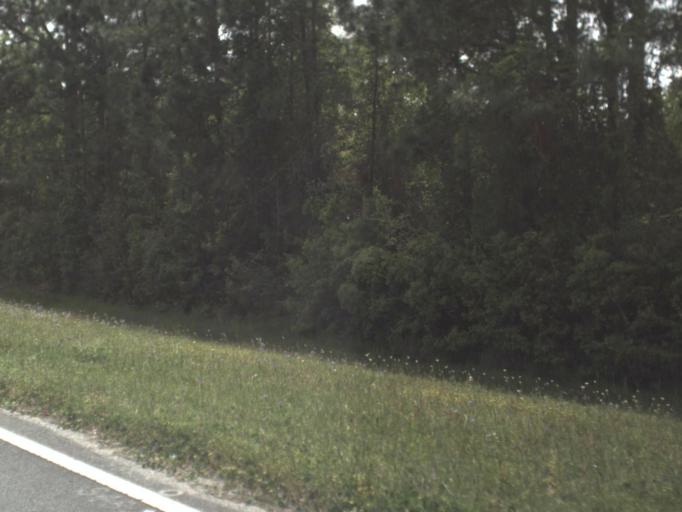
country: US
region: Florida
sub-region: Escambia County
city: Myrtle Grove
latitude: 30.3524
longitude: -87.3548
